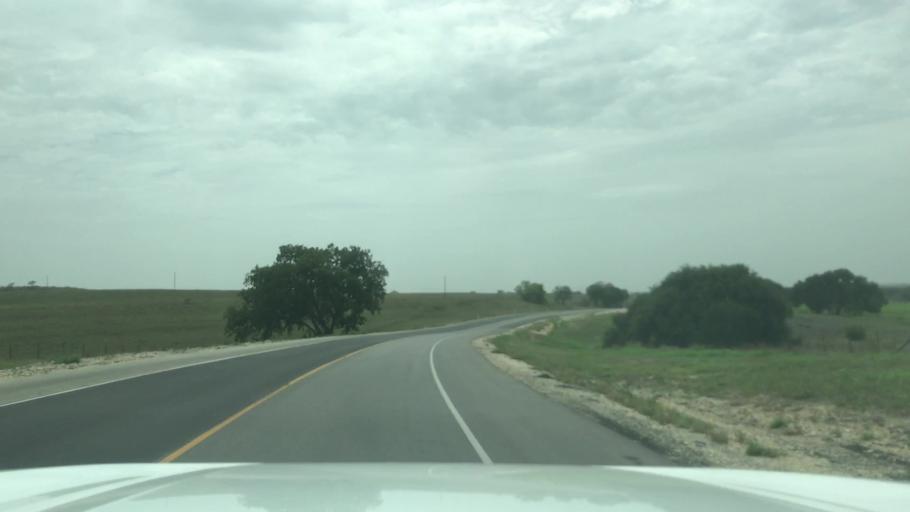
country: US
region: Texas
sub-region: Erath County
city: Dublin
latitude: 32.0724
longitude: -98.2234
